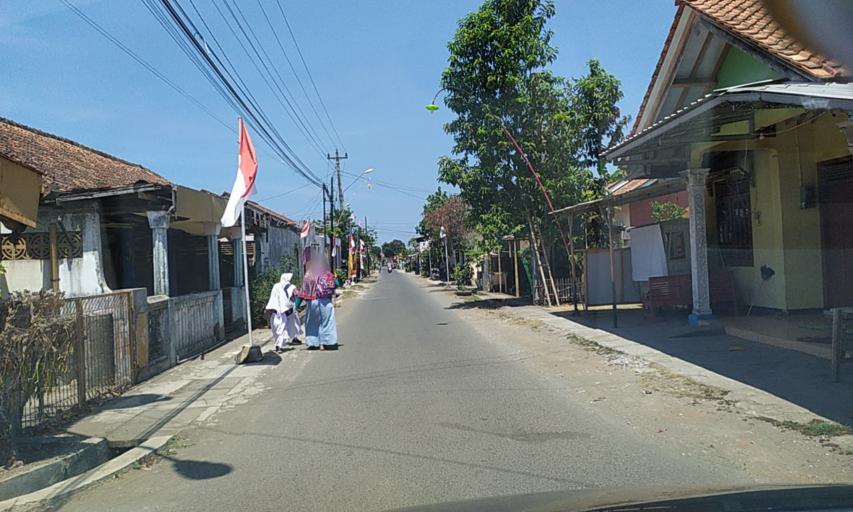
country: ID
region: Central Java
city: Rejanegara
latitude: -7.6803
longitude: 109.0556
